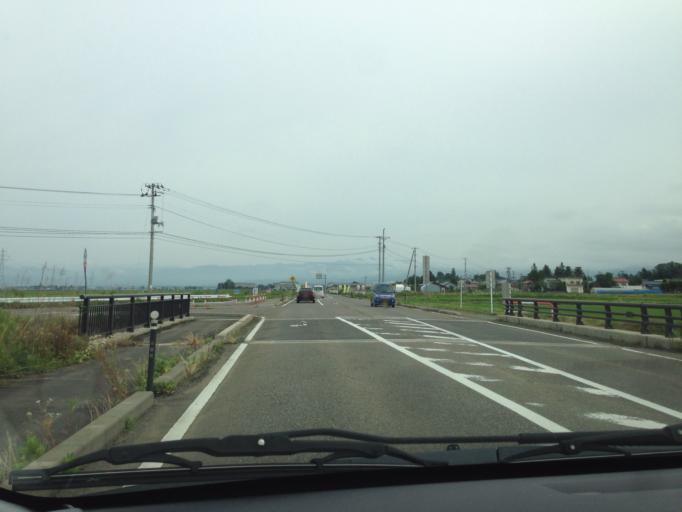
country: JP
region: Fukushima
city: Kitakata
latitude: 37.5949
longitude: 139.9122
